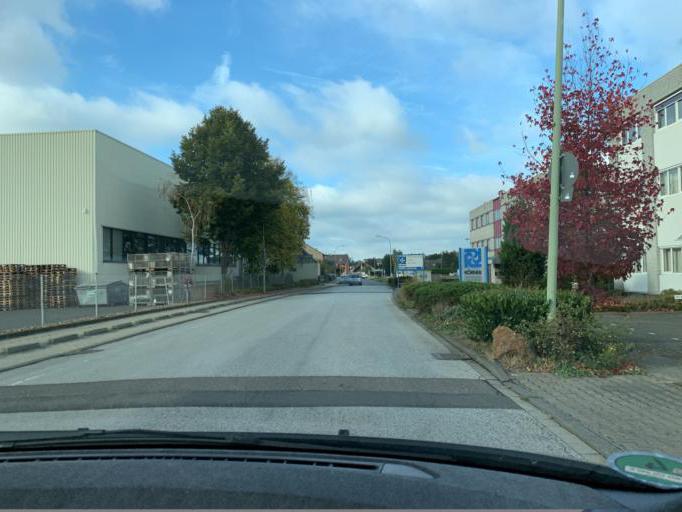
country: DE
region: North Rhine-Westphalia
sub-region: Regierungsbezirk Koln
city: Niederzier
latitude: 50.8487
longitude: 6.4547
